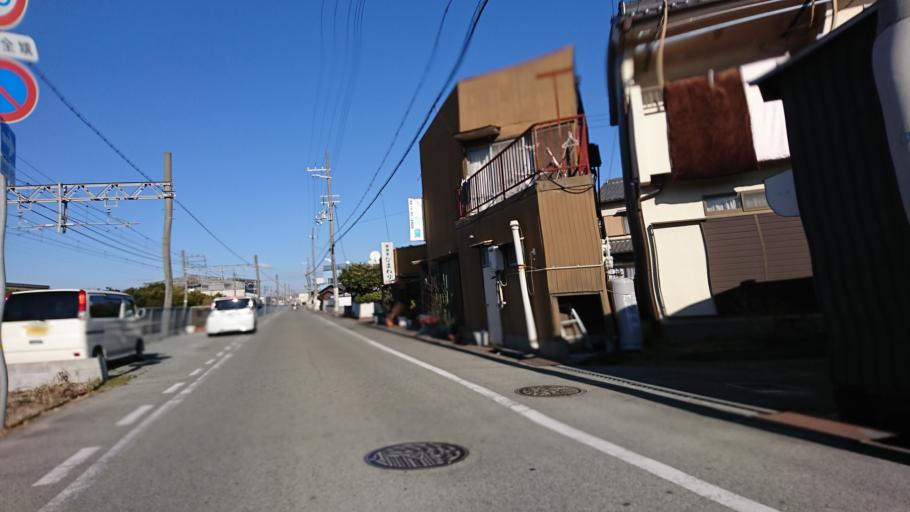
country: JP
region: Hyogo
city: Kakogawacho-honmachi
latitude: 34.7625
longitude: 134.7898
